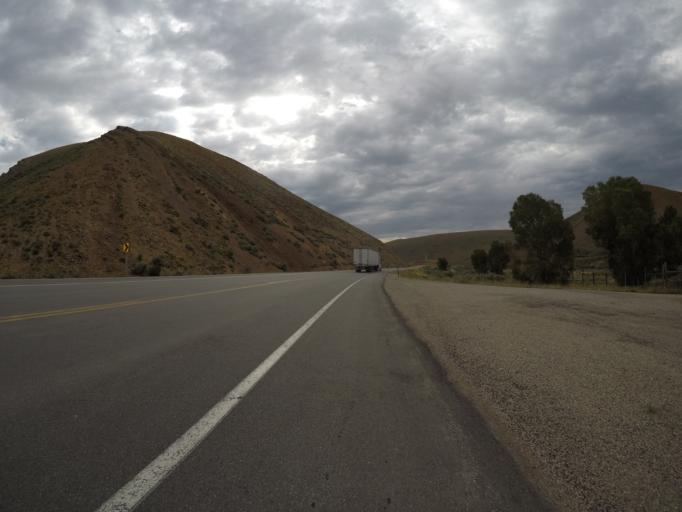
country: US
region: Wyoming
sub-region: Lincoln County
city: Kemmerer
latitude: 41.8245
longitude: -110.8251
